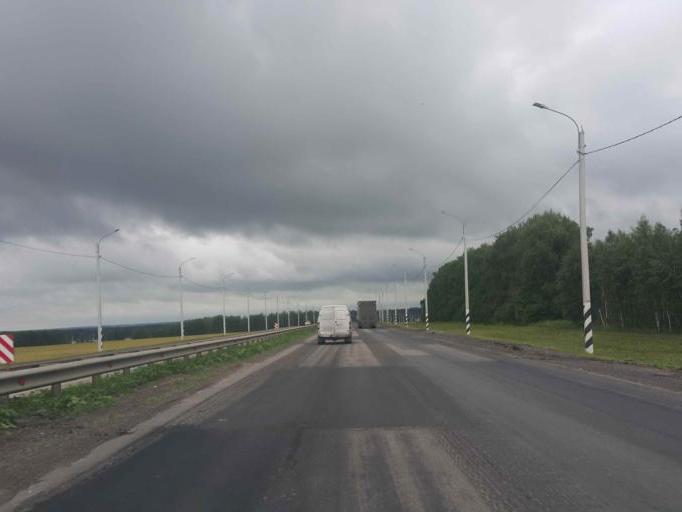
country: RU
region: Tambov
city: Selezni
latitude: 52.7410
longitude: 41.2167
